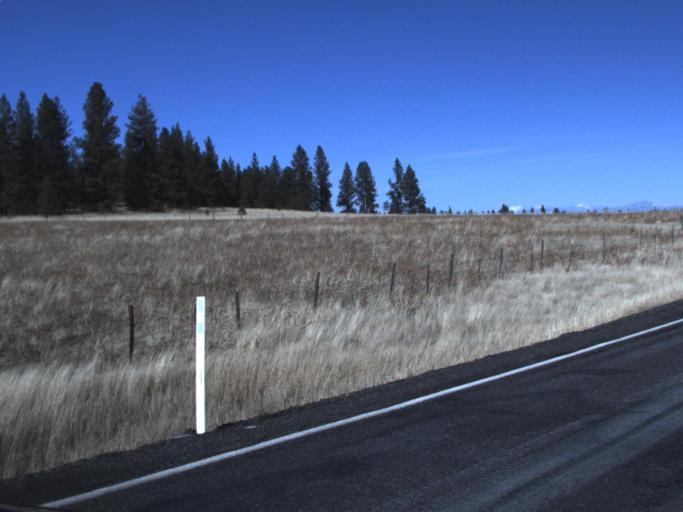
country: US
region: Washington
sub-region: Asotin County
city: Asotin
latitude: 46.1138
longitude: -117.1367
